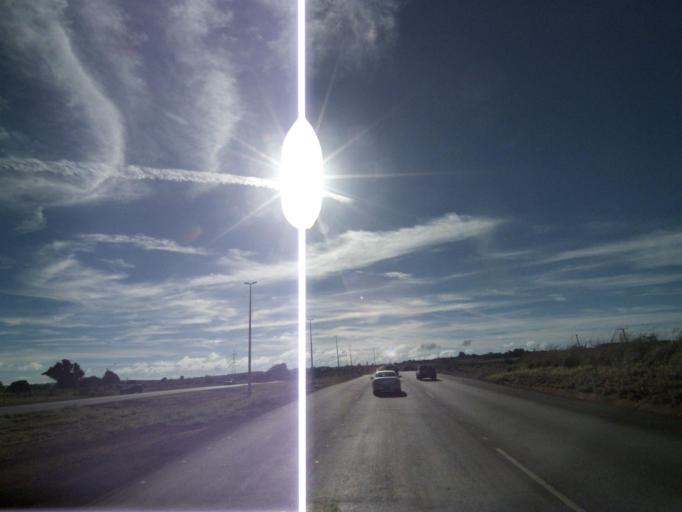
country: BR
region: Federal District
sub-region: Brasilia
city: Brasilia
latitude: -15.7893
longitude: -48.2182
